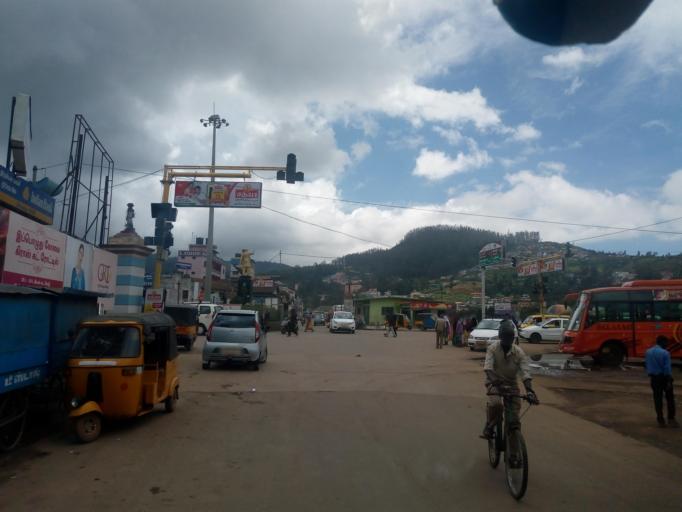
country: IN
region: Tamil Nadu
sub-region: Nilgiri
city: Ooty
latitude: 11.4044
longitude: 76.6963
